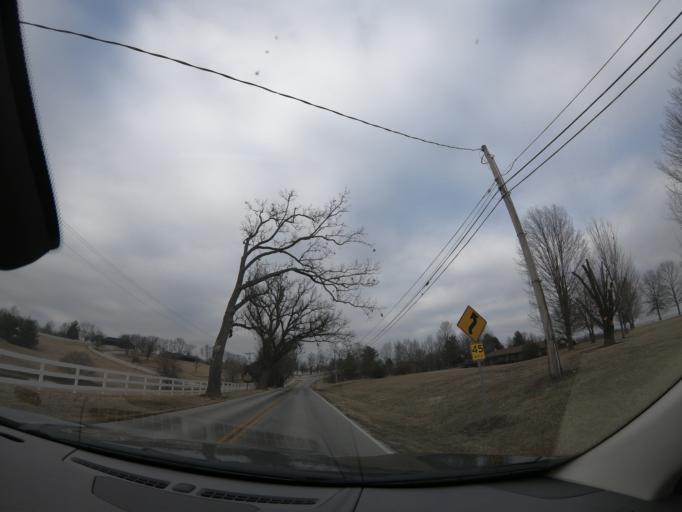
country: US
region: Kentucky
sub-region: Spencer County
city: Taylorsville
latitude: 37.9246
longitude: -85.3156
